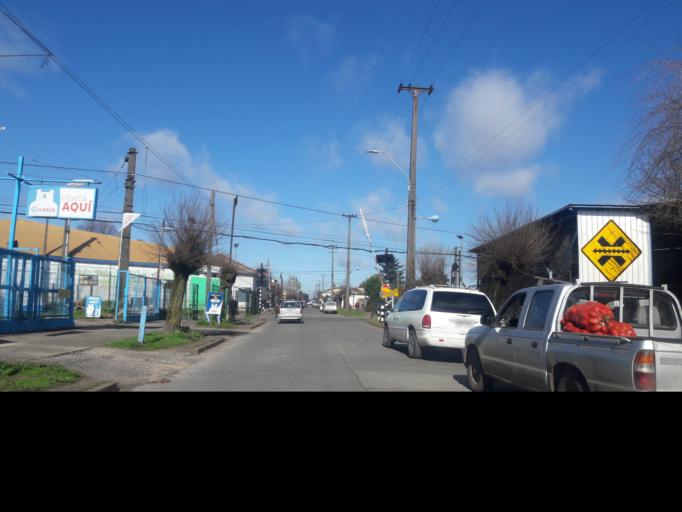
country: CL
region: Araucania
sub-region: Provincia de Malleco
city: Victoria
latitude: -38.2350
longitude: -72.3295
